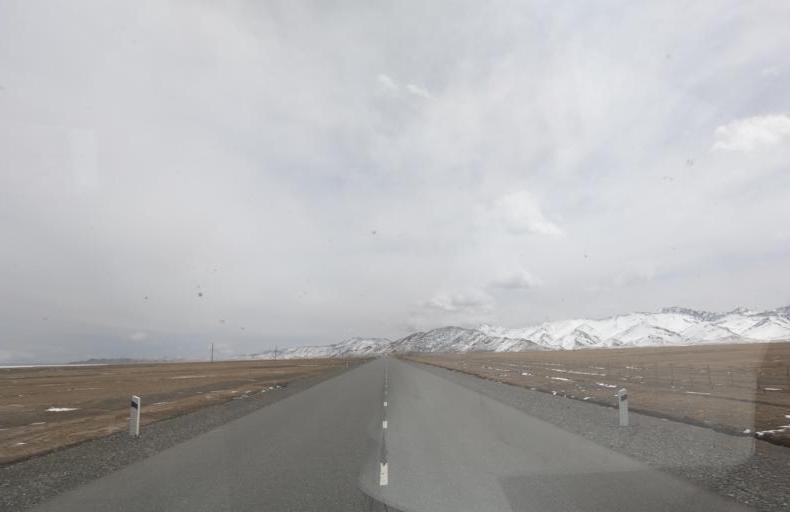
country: KG
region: Naryn
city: Baetov
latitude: 40.5517
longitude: 75.2238
